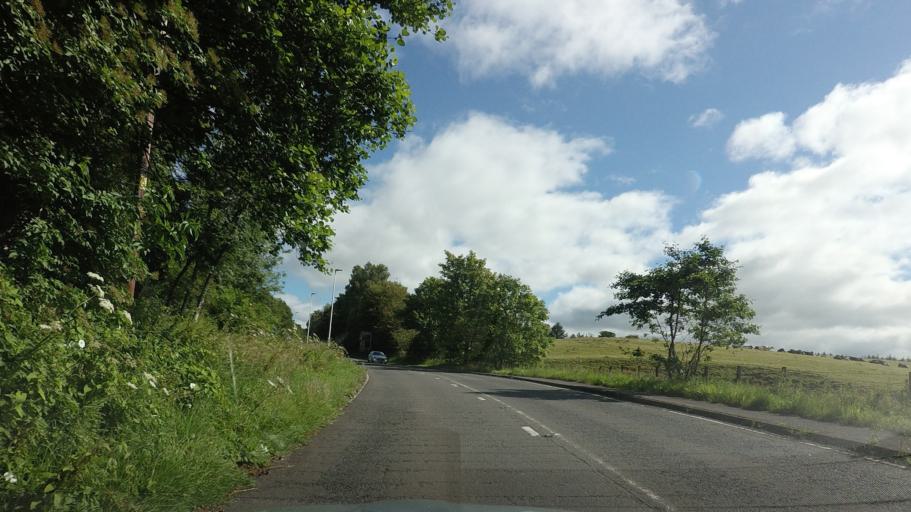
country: GB
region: Scotland
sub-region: Stirling
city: Killearn
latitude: 56.0592
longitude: -4.4525
